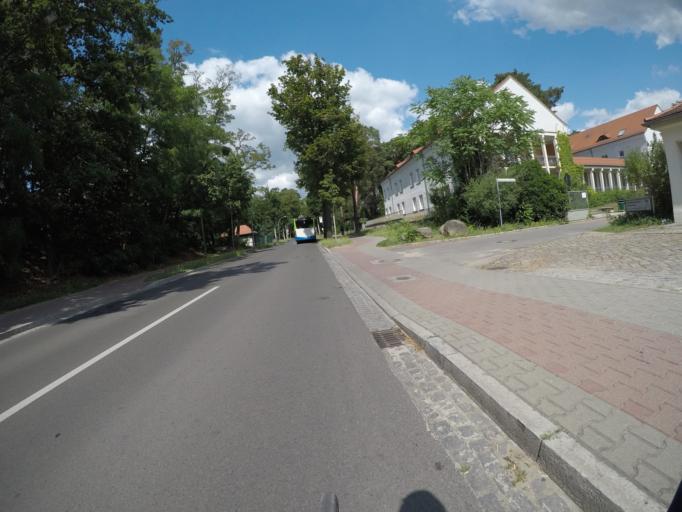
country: DE
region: Brandenburg
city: Stahnsdorf
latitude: 52.3971
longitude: 13.2080
